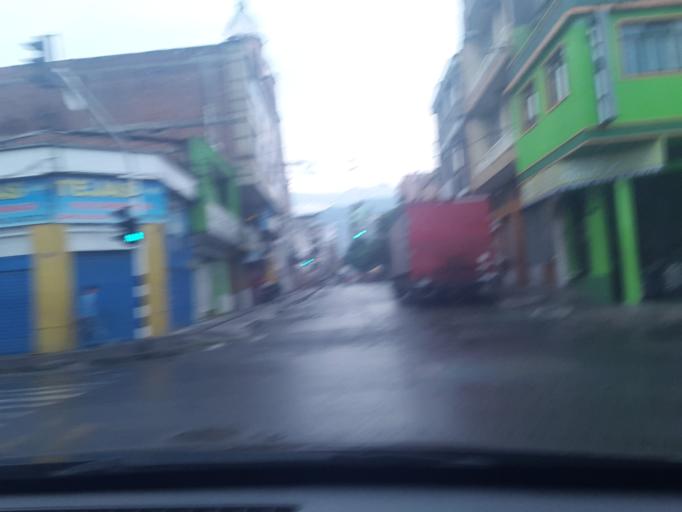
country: CO
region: Quindio
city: Armenia
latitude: 4.5377
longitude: -75.6727
